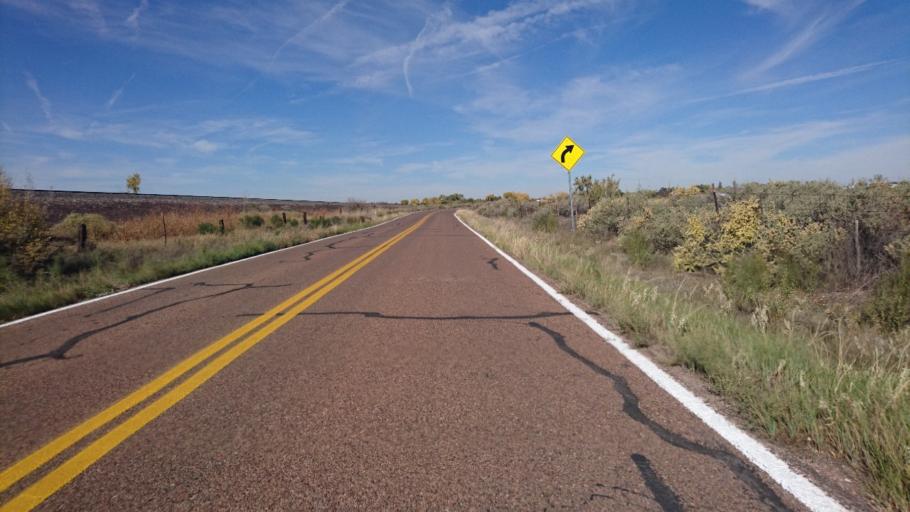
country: US
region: Arizona
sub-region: Navajo County
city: Joseph City
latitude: 34.9471
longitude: -110.3296
